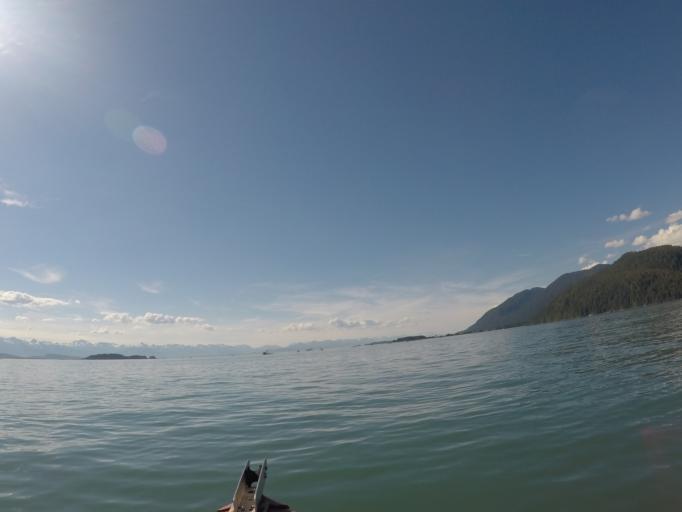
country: US
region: Alaska
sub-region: Juneau City and Borough
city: Juneau
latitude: 58.4928
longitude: -134.8124
